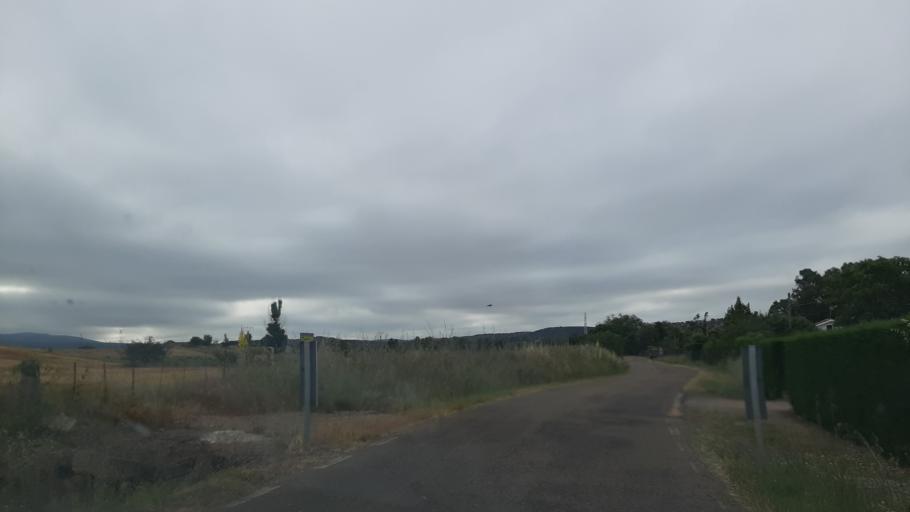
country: ES
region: Castille and Leon
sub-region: Provincia de Salamanca
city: Ciudad Rodrigo
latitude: 40.5674
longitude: -6.4884
